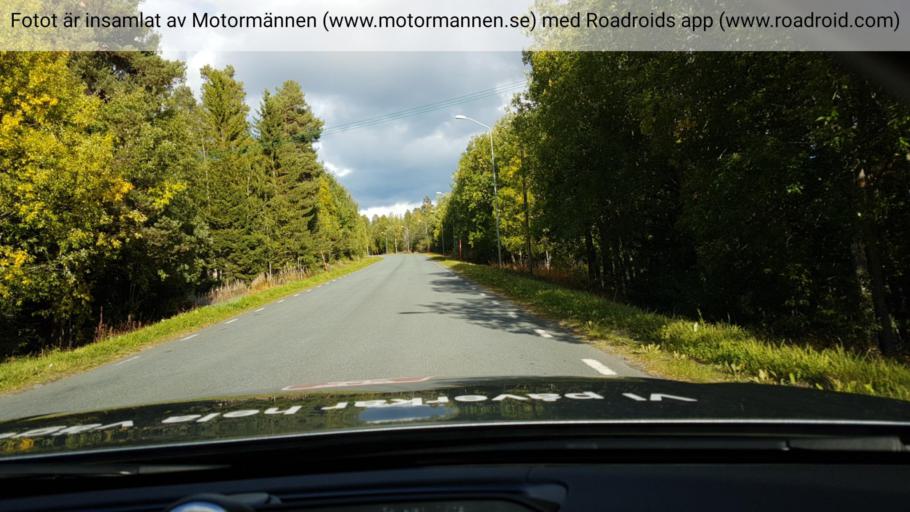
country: SE
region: Jaemtland
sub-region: Are Kommun
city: Jarpen
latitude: 63.3073
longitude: 13.6774
